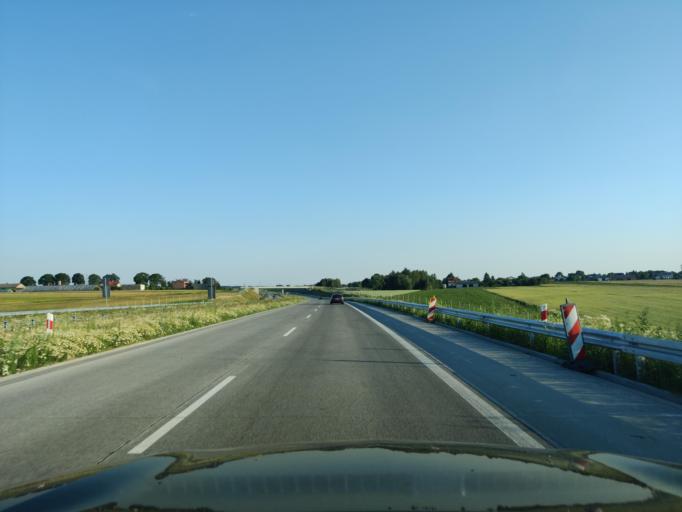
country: PL
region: Masovian Voivodeship
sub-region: Powiat mlawski
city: Mlawa
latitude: 53.1199
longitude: 20.4102
